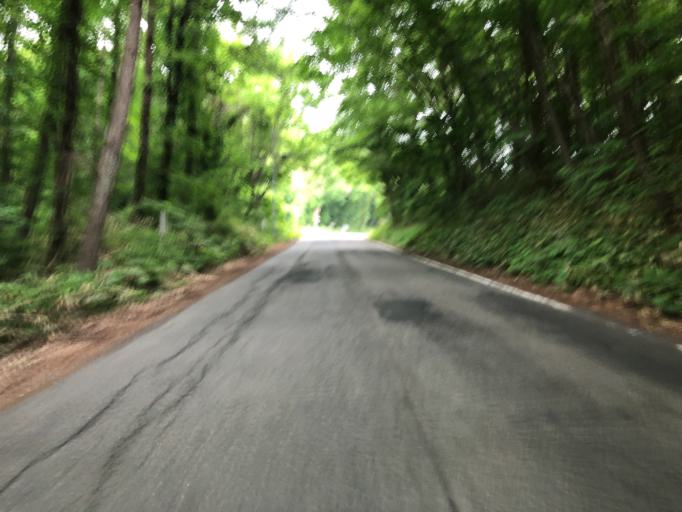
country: JP
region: Fukushima
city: Funehikimachi-funehiki
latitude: 37.3841
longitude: 140.7079
